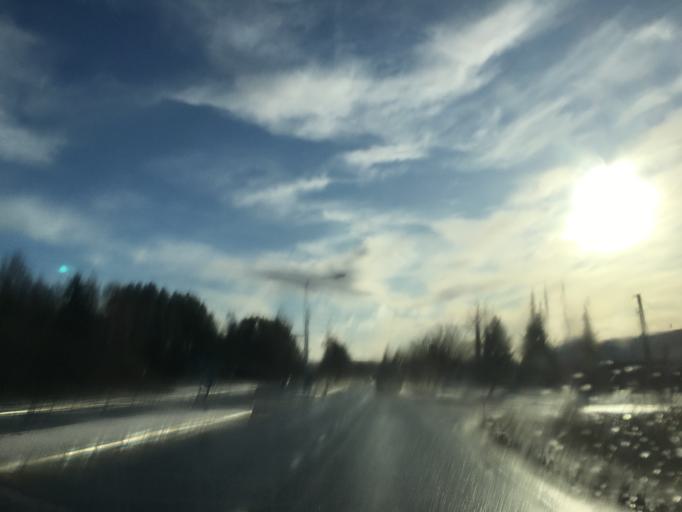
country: FI
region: Varsinais-Suomi
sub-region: Turku
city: Raisio
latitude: 60.4749
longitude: 22.2056
